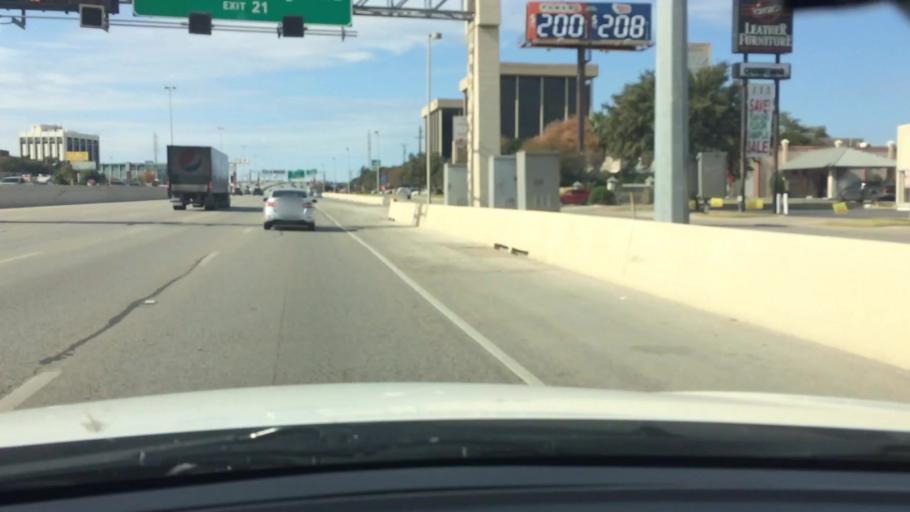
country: US
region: Texas
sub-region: Bexar County
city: Alamo Heights
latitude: 29.5164
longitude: -98.4572
